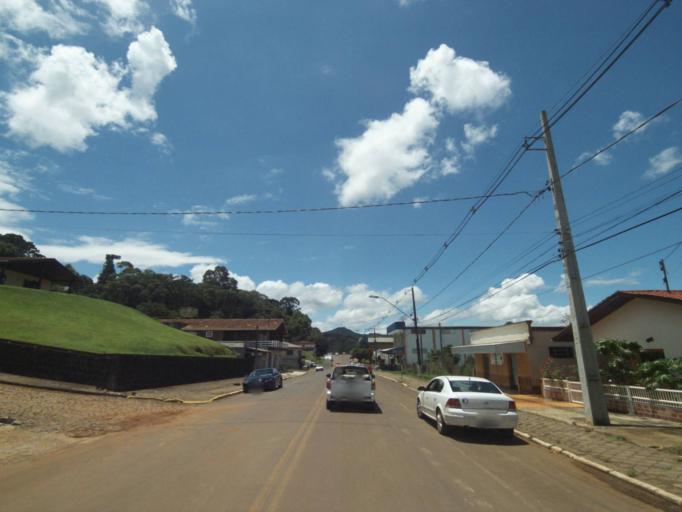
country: BR
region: Parana
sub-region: Uniao Da Vitoria
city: Uniao da Vitoria
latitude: -26.1634
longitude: -51.5549
